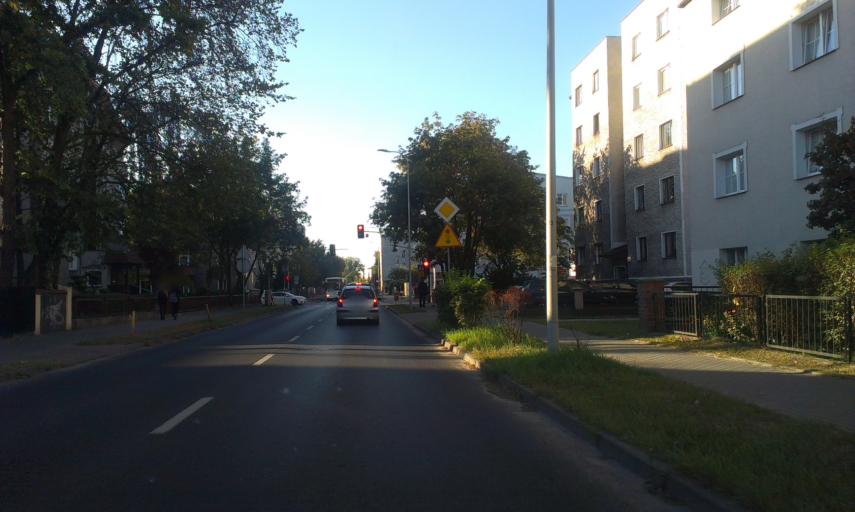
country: PL
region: Kujawsko-Pomorskie
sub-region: Torun
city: Torun
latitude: 53.0231
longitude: 18.6017
